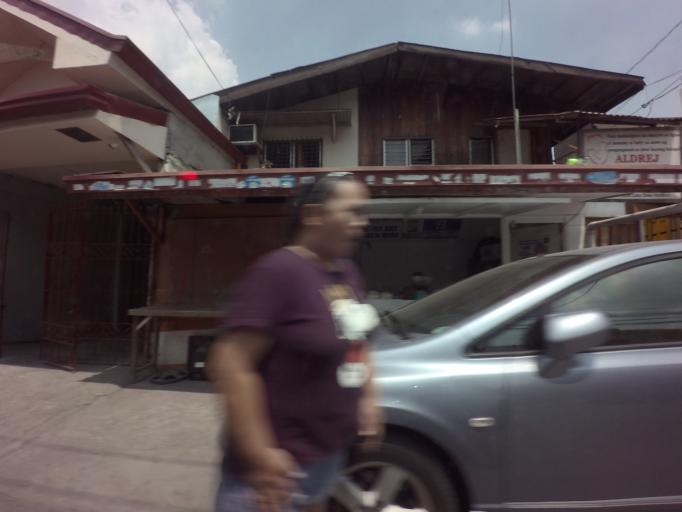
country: PH
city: Sambayanihan People's Village
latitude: 14.4419
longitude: 121.0505
